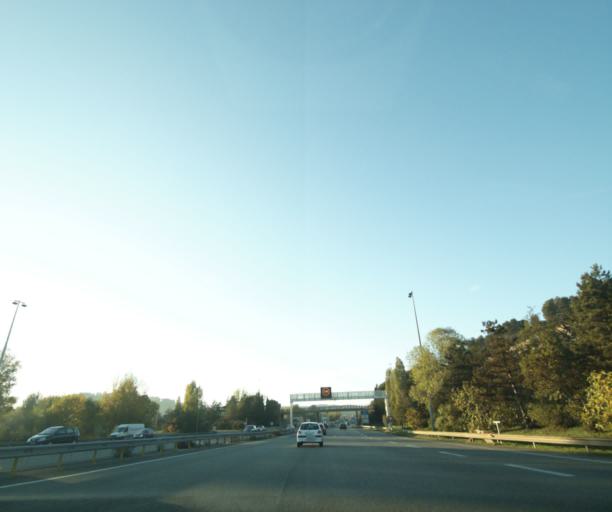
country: FR
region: Provence-Alpes-Cote d'Azur
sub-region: Departement des Bouches-du-Rhone
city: Chateauneuf-le-Rouge
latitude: 43.4841
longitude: 5.5374
